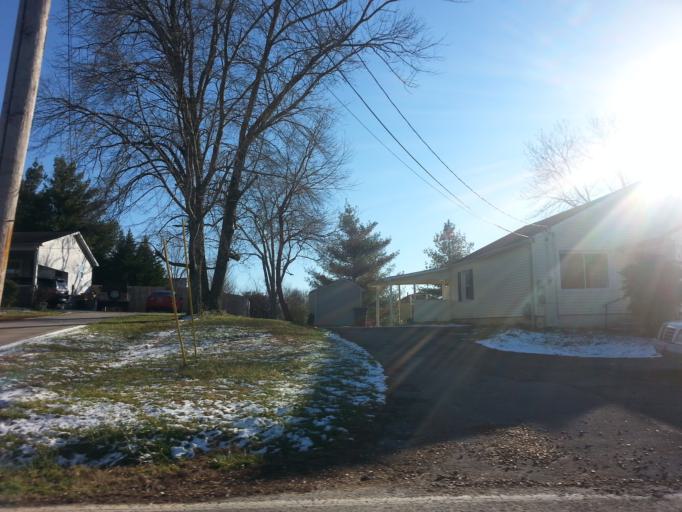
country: US
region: Tennessee
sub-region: Blount County
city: Louisville
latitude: 35.9457
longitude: -84.0443
